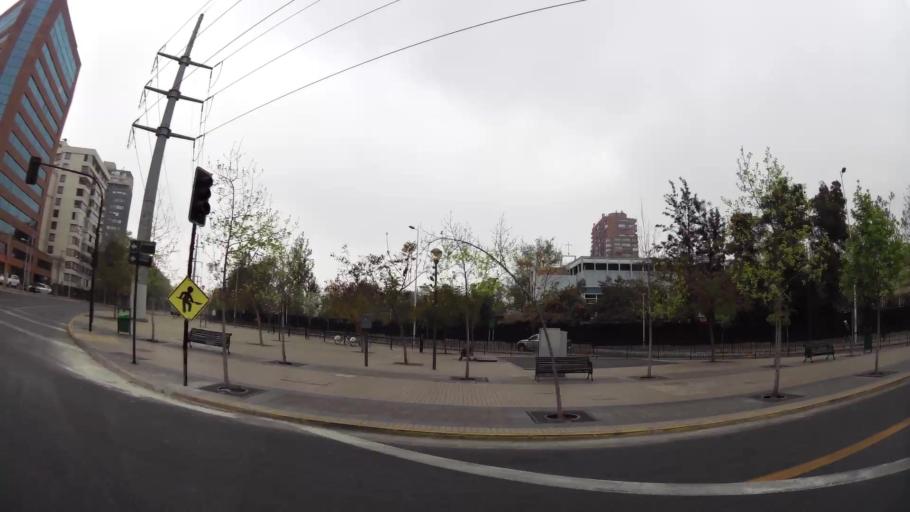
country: CL
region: Santiago Metropolitan
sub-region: Provincia de Santiago
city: Villa Presidente Frei, Nunoa, Santiago, Chile
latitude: -33.4085
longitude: -70.5659
